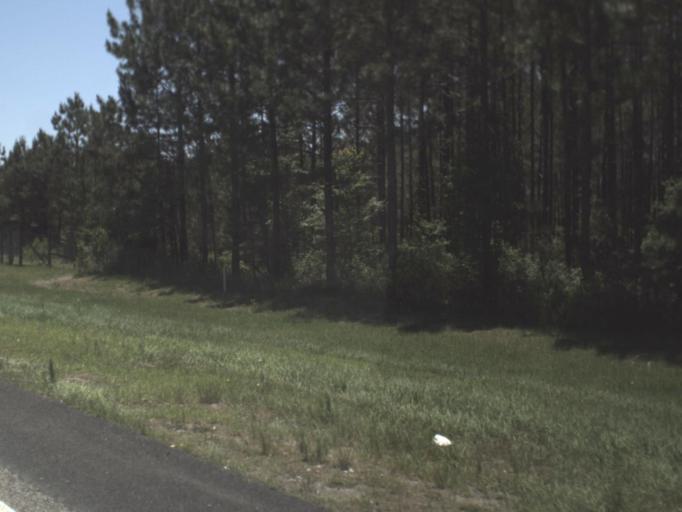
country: US
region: Florida
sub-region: Clay County
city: Lakeside
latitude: 30.1928
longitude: -81.8377
